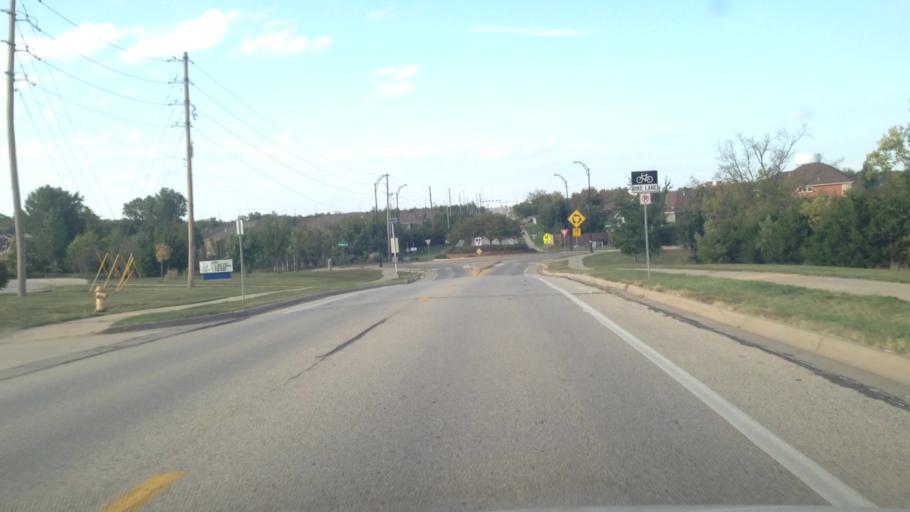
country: US
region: Kansas
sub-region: Douglas County
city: Lawrence
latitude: 38.9631
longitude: -95.3256
